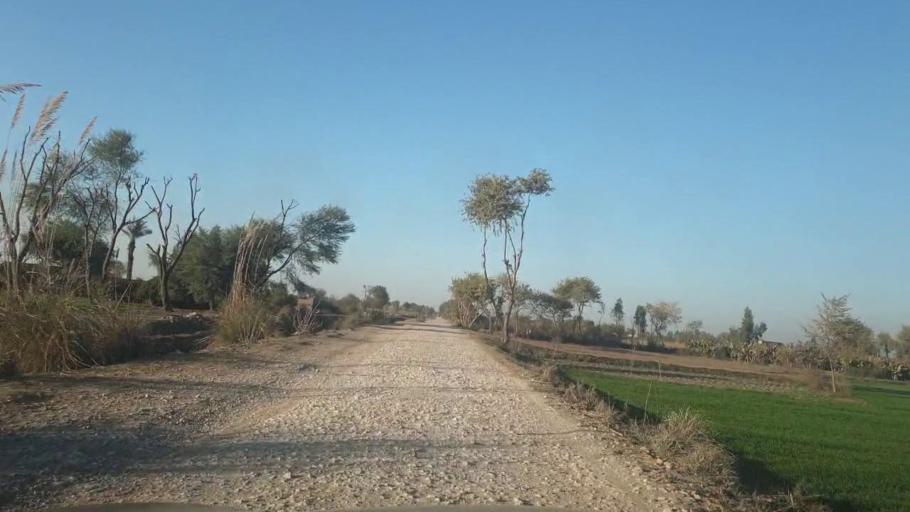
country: PK
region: Sindh
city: Ghotki
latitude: 27.9990
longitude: 69.2712
